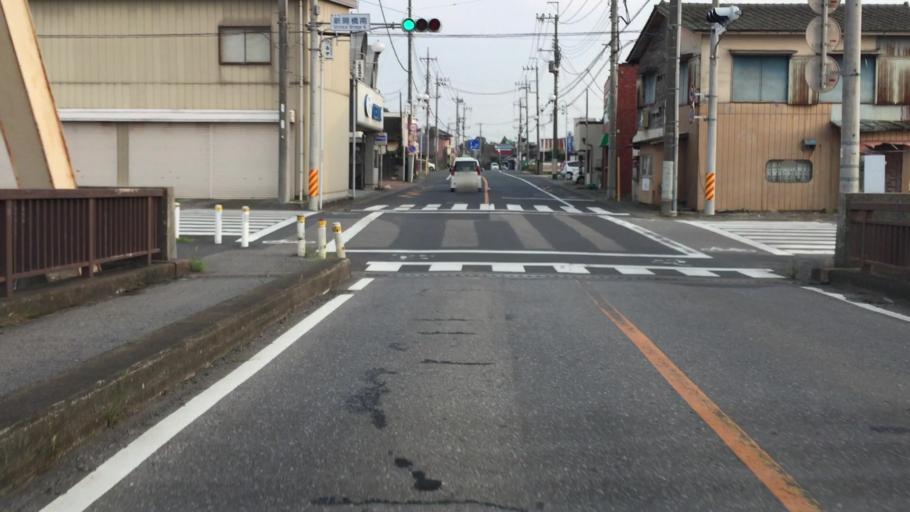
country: JP
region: Tochigi
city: Fujioka
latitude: 36.2638
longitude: 139.6500
